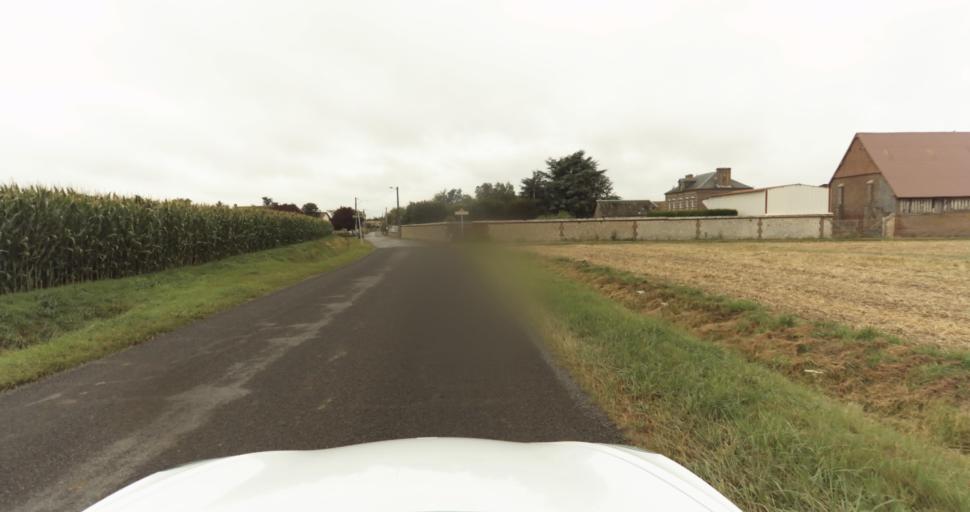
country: FR
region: Haute-Normandie
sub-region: Departement de l'Eure
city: Claville
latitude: 49.0906
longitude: 1.0544
